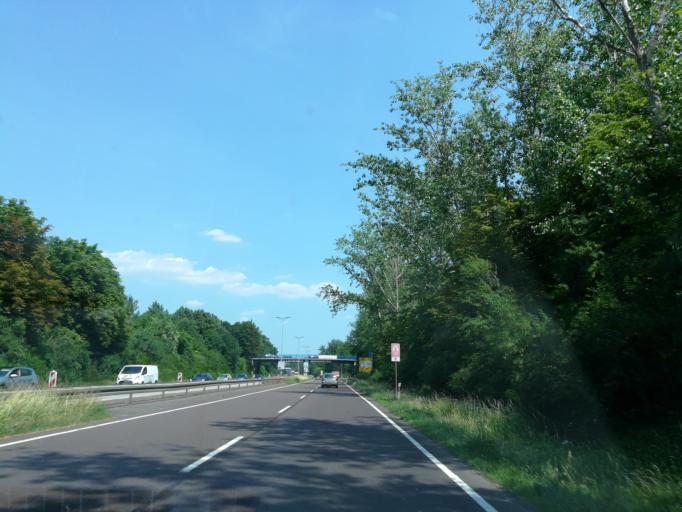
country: DE
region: Saxony-Anhalt
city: Diesdorf
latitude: 52.0812
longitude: 11.5875
